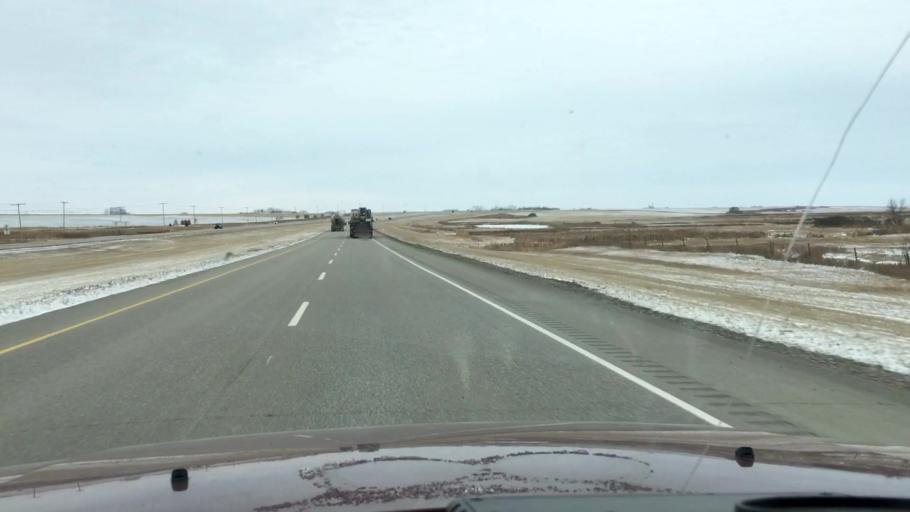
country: CA
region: Saskatchewan
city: Watrous
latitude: 51.2407
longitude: -105.9654
